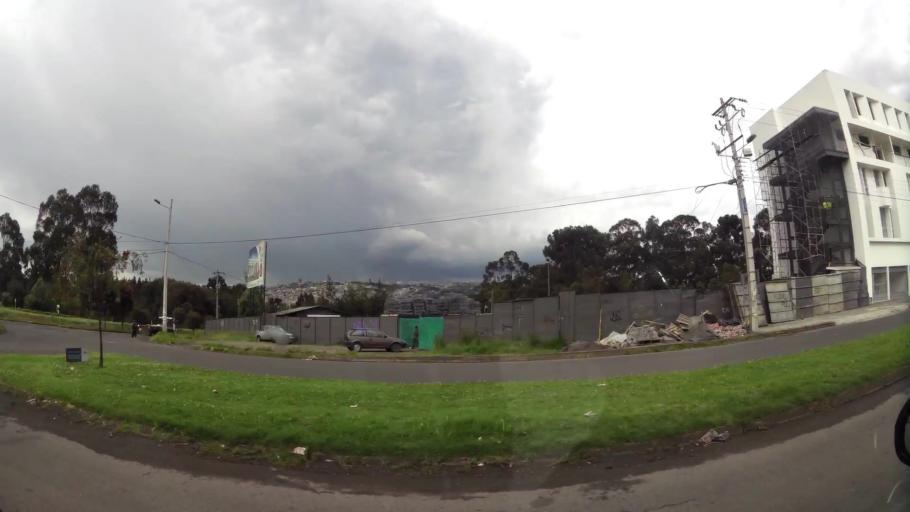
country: EC
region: Pichincha
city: Quito
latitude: -0.2899
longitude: -78.5504
